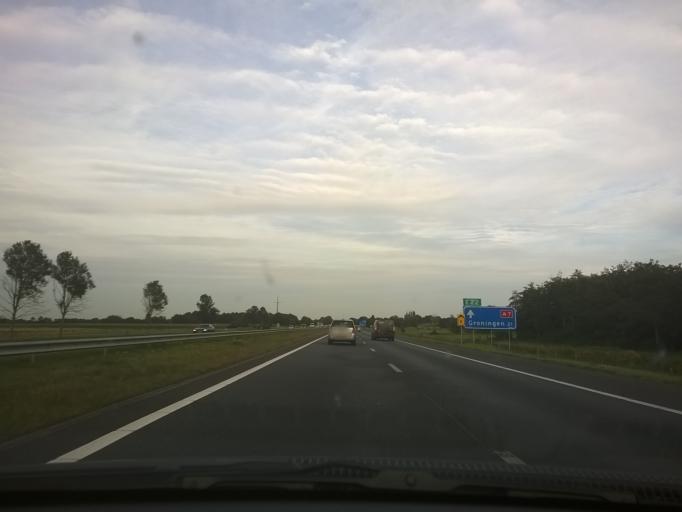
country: NL
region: Groningen
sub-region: Gemeente Grootegast
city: Grootegast
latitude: 53.1490
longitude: 6.2540
